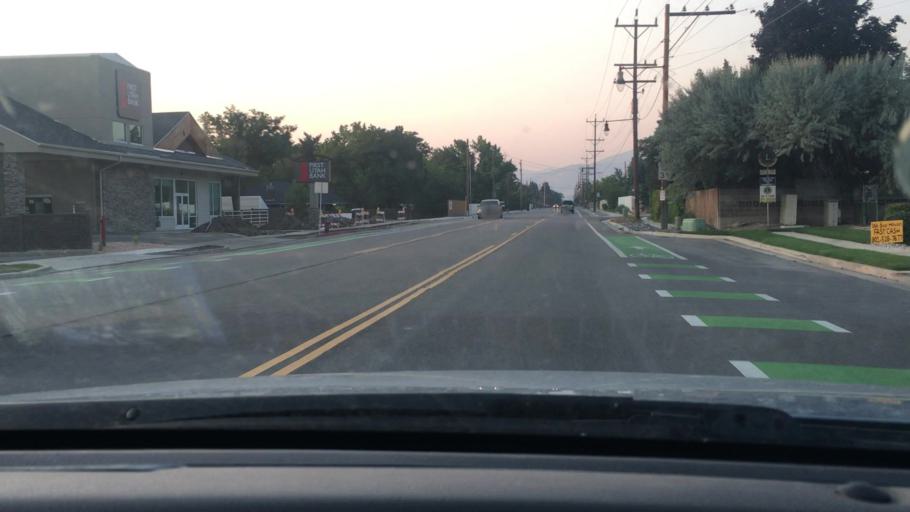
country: US
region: Utah
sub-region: Salt Lake County
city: East Millcreek
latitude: 40.6876
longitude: -111.8245
